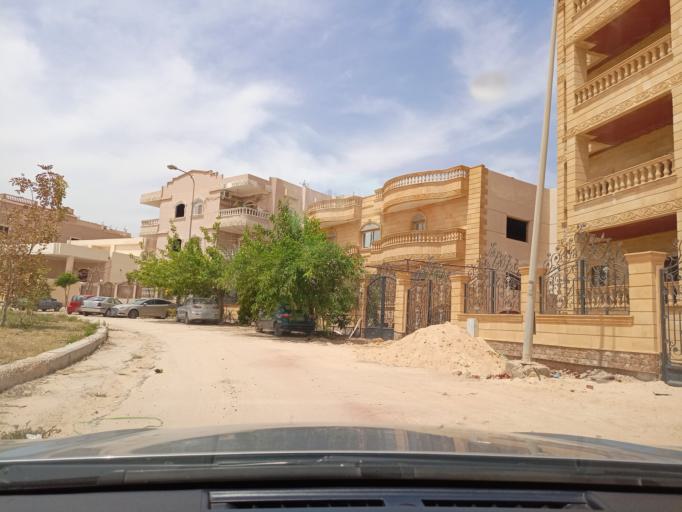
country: EG
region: Muhafazat al Qalyubiyah
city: Al Khankah
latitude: 30.2282
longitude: 31.4882
